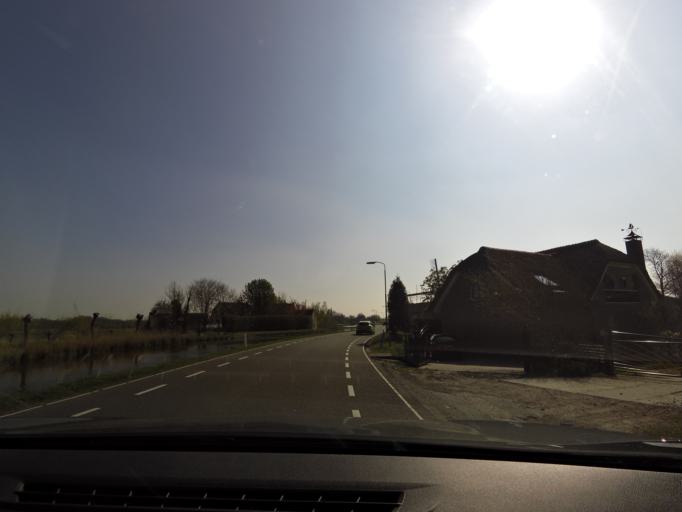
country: NL
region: South Holland
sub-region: Gemeente Maassluis
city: Maassluis
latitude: 51.9449
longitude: 4.2756
